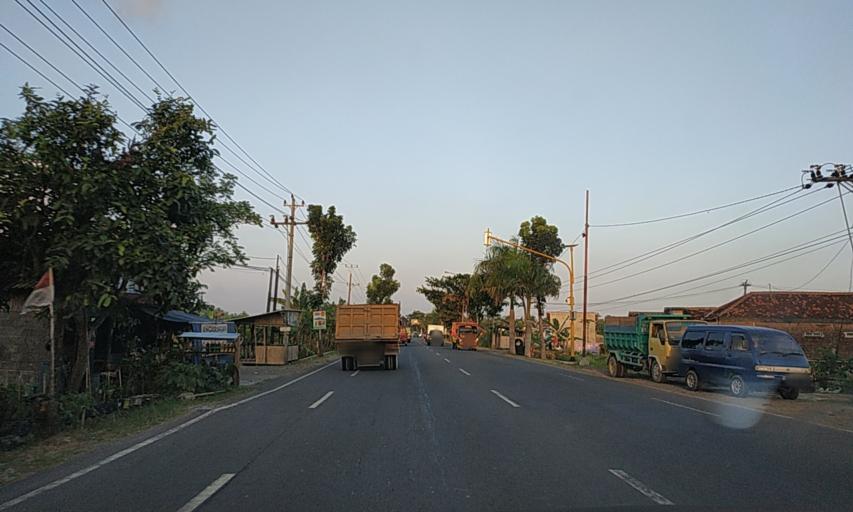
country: ID
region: Daerah Istimewa Yogyakarta
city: Srandakan
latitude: -7.8881
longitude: 110.0928
